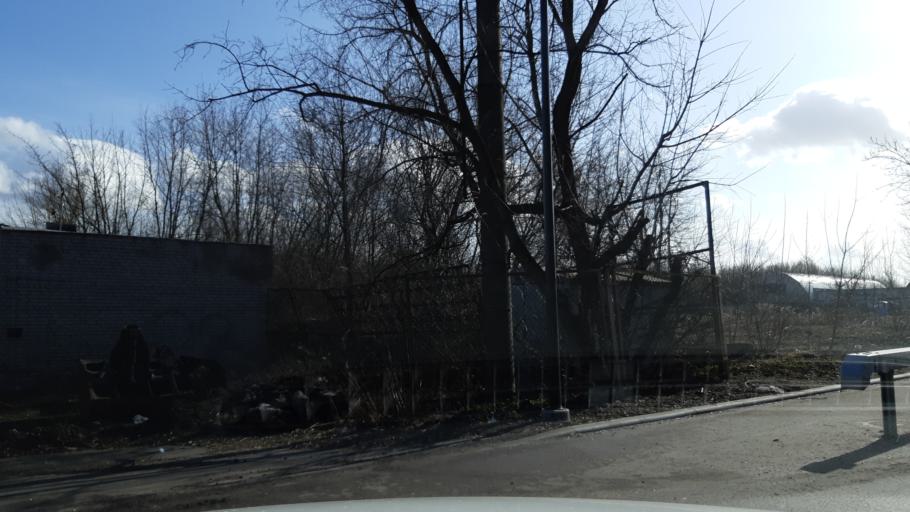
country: LT
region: Kauno apskritis
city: Dainava (Kaunas)
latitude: 54.8775
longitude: 23.9576
